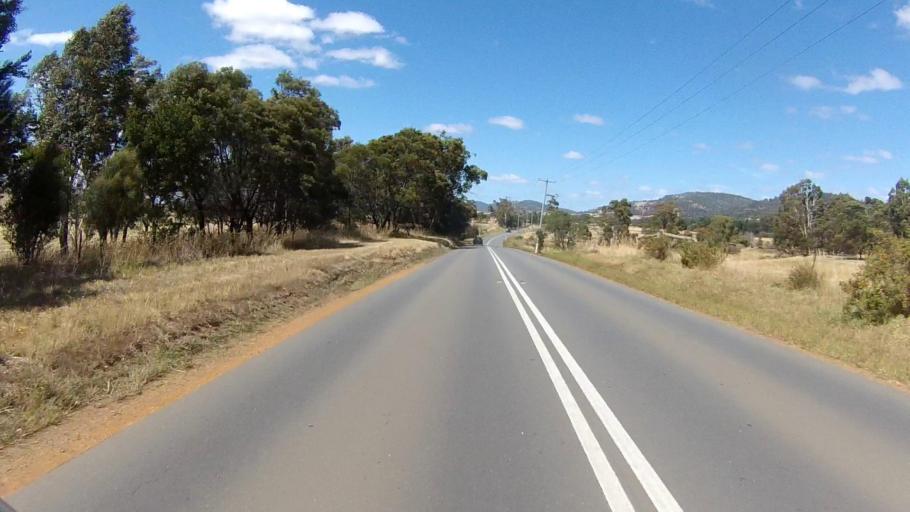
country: AU
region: Tasmania
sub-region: Clarence
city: Cambridge
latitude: -42.7655
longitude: 147.4153
